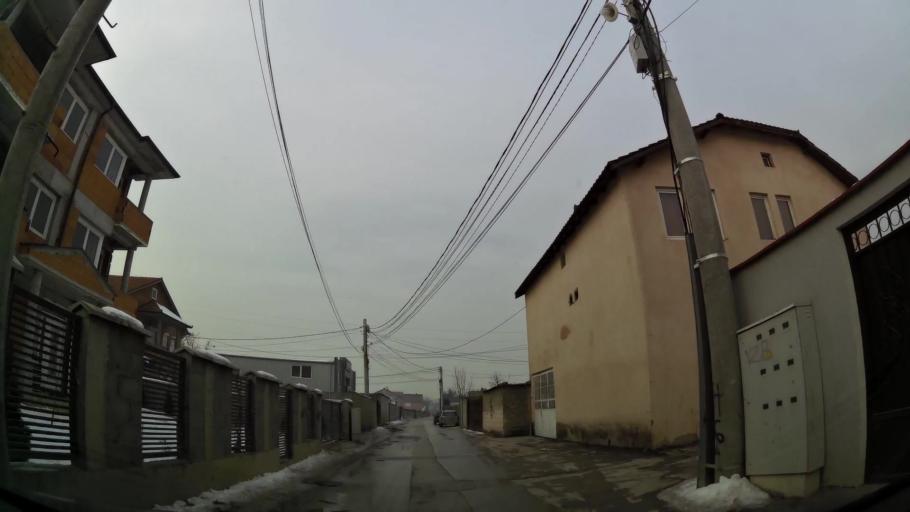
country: MK
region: Suto Orizari
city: Suto Orizare
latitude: 42.0285
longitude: 21.4248
